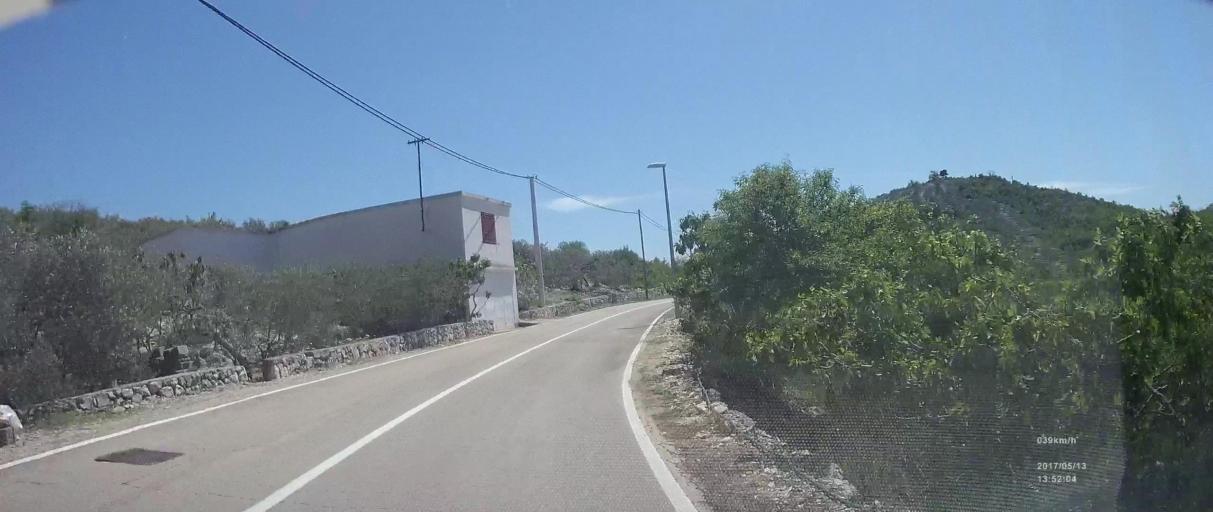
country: HR
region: Sibensko-Kniniska
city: Primosten
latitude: 43.6094
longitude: 15.9959
